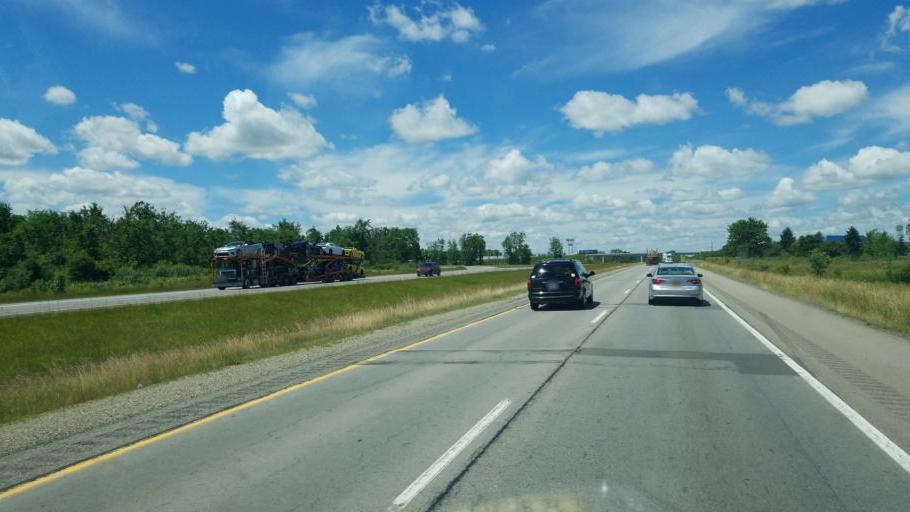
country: US
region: Michigan
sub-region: Livingston County
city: Fowlerville
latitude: 42.6467
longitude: -84.0664
